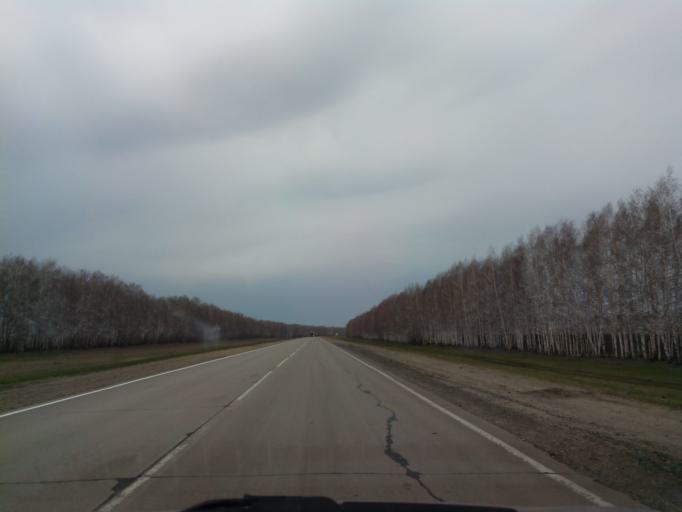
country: RU
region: Tambov
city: Znamenka
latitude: 52.2716
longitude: 41.4904
